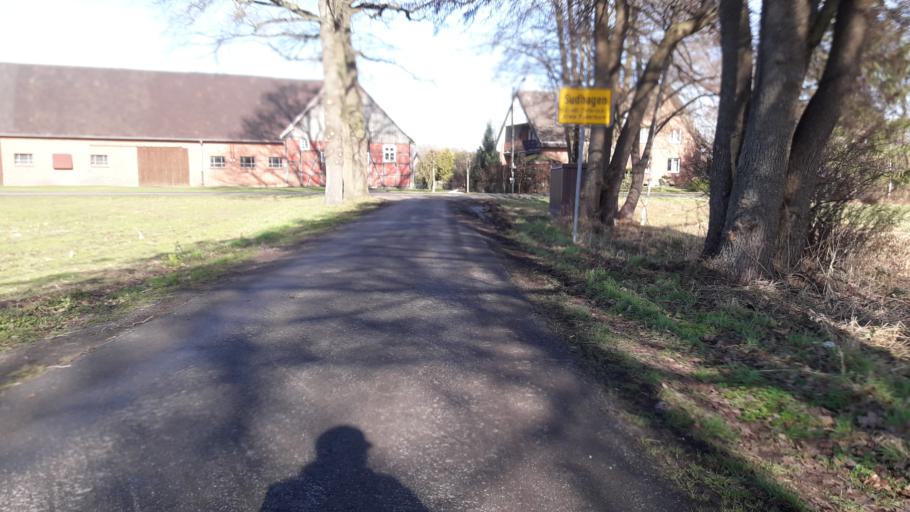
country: DE
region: North Rhine-Westphalia
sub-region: Regierungsbezirk Detmold
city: Delbruck
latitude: 51.7441
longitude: 8.5016
